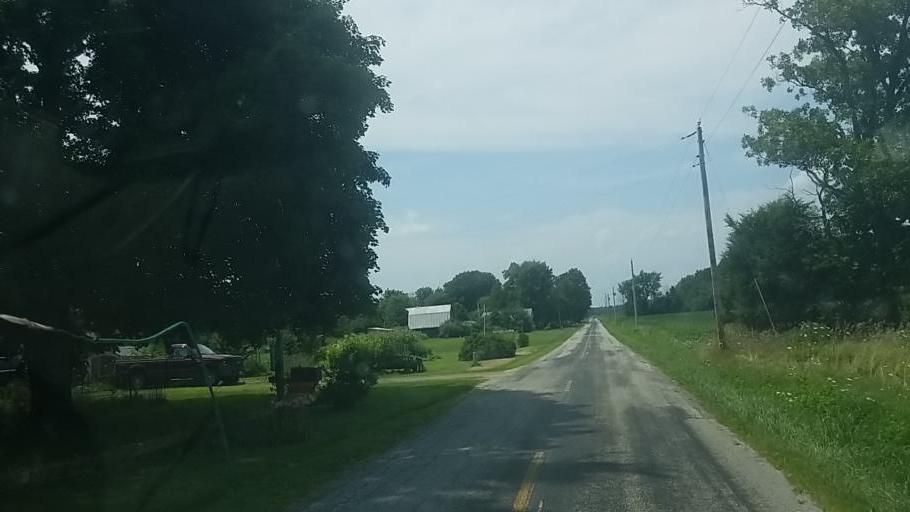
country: US
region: Ohio
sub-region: Union County
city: Richwood
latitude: 40.6074
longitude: -83.3486
